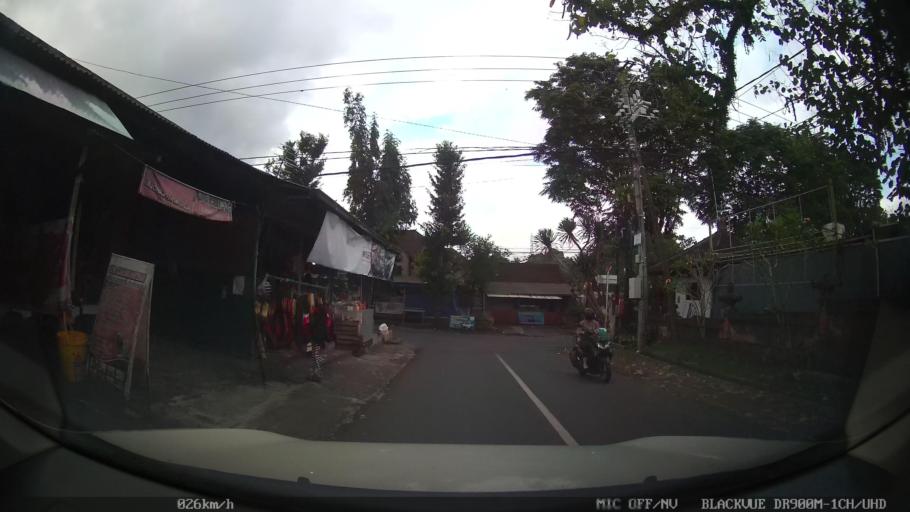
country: ID
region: Bali
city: Tabanan
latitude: -8.5419
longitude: 115.1223
